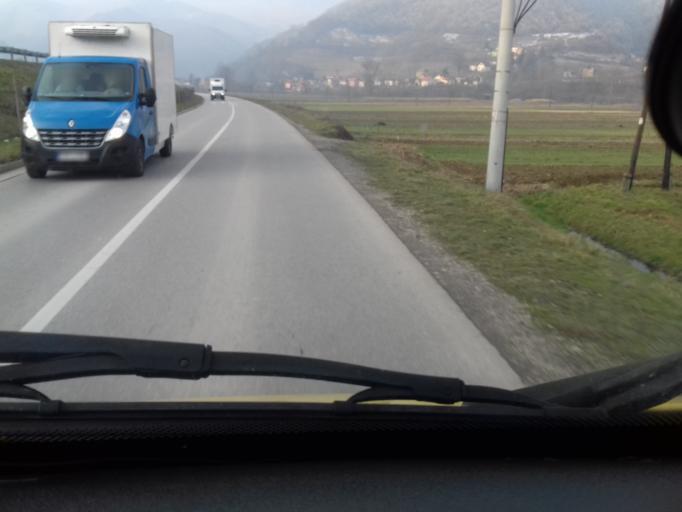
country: BA
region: Federation of Bosnia and Herzegovina
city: Dobrinje
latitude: 44.0441
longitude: 18.1197
